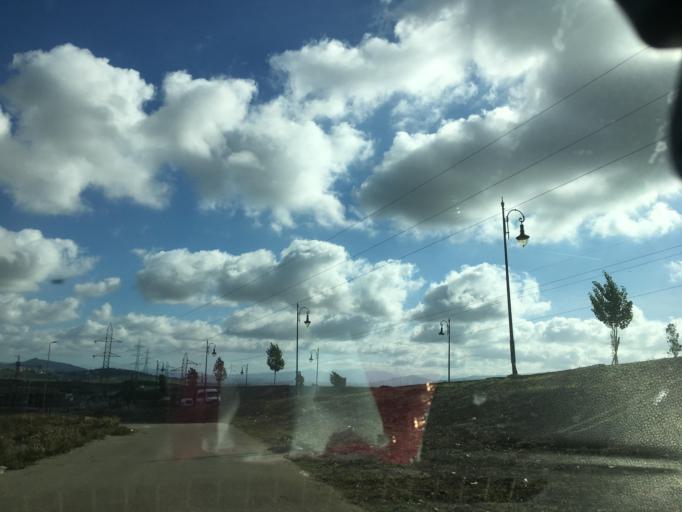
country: MA
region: Tanger-Tetouan
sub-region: Tanger-Assilah
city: Tangier
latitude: 35.7092
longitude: -5.8182
